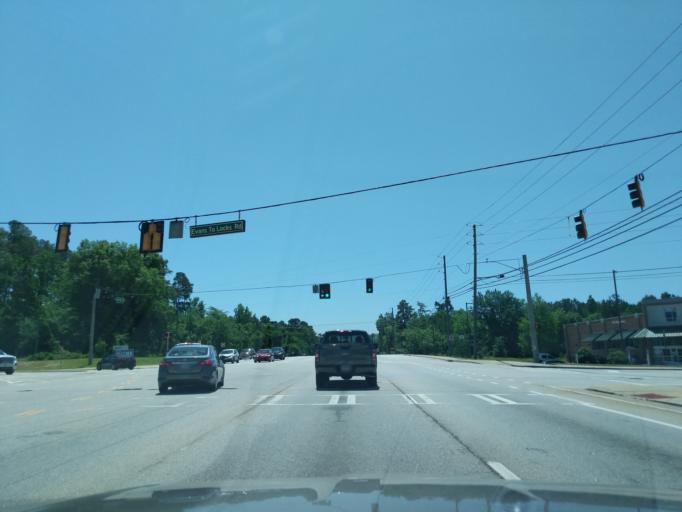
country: US
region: Georgia
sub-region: Columbia County
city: Martinez
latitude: 33.5503
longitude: -82.0901
